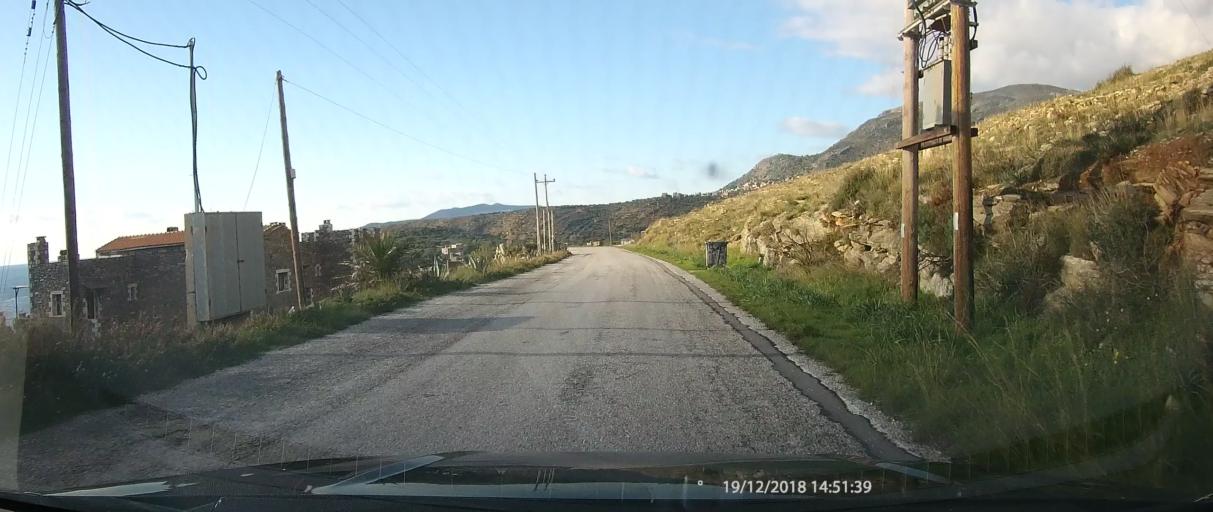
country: GR
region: Peloponnese
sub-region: Nomos Lakonias
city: Gytheio
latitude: 36.4590
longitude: 22.4461
